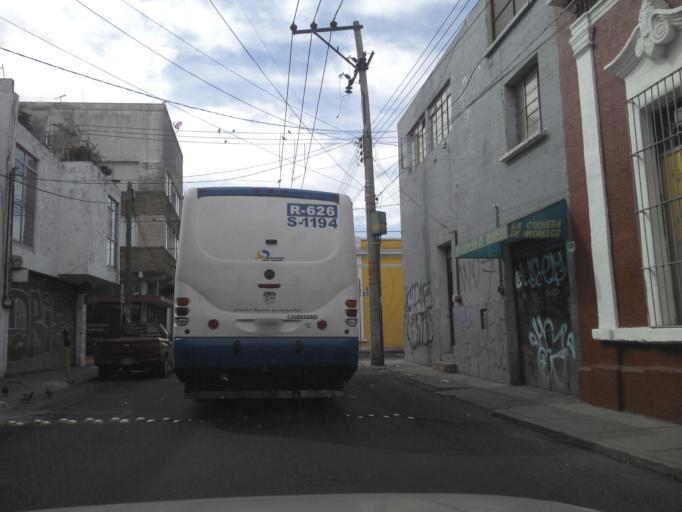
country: MX
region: Jalisco
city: Guadalajara
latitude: 20.6762
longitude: -103.3611
